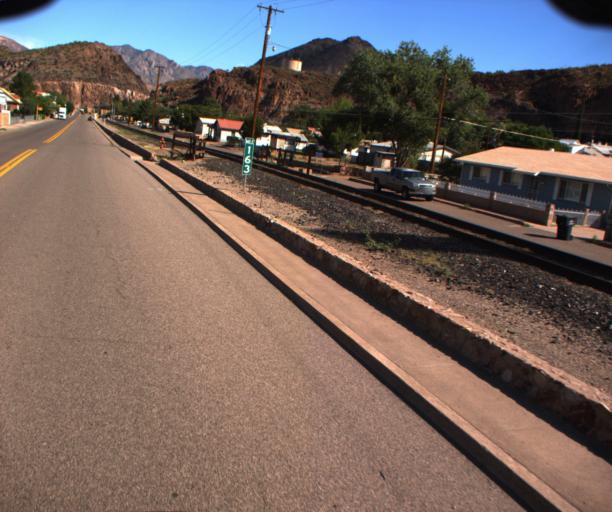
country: US
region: Arizona
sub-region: Greenlee County
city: Clifton
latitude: 33.0446
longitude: -109.2921
